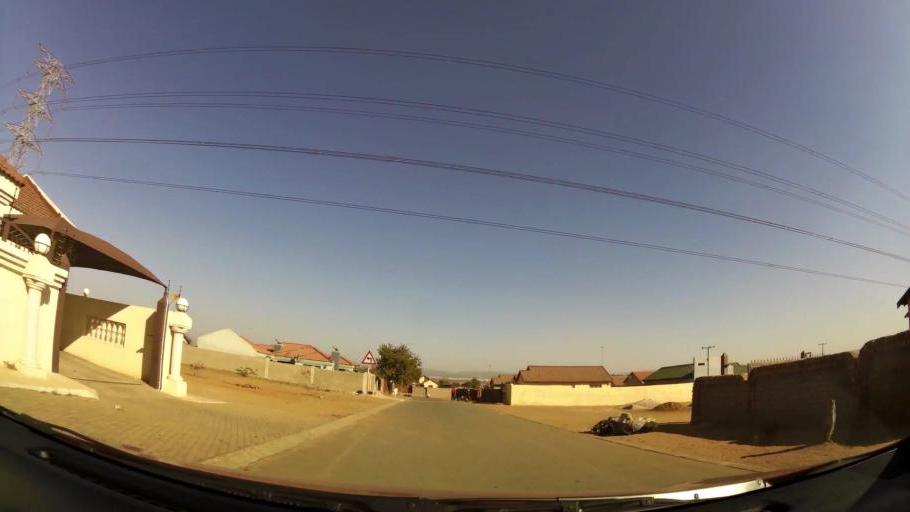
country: ZA
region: Gauteng
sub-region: City of Tshwane Metropolitan Municipality
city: Mabopane
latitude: -25.5771
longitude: 28.0935
